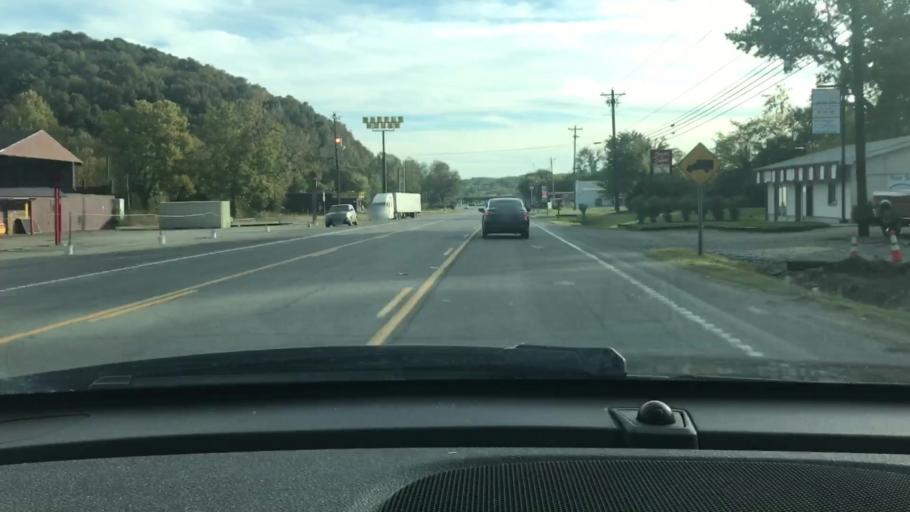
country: US
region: Tennessee
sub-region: Sumner County
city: Millersville
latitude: 36.3529
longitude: -86.7147
